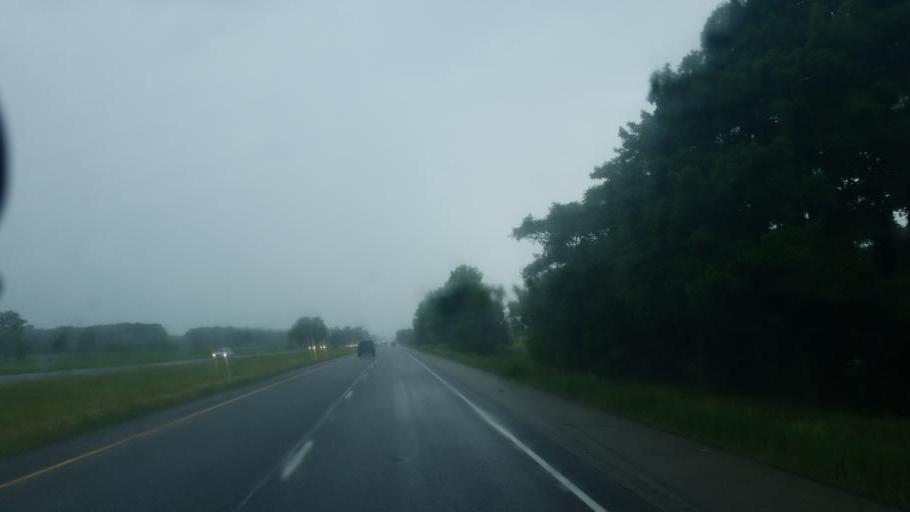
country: US
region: Indiana
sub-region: Whitley County
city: Columbia City
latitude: 41.1325
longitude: -85.4006
